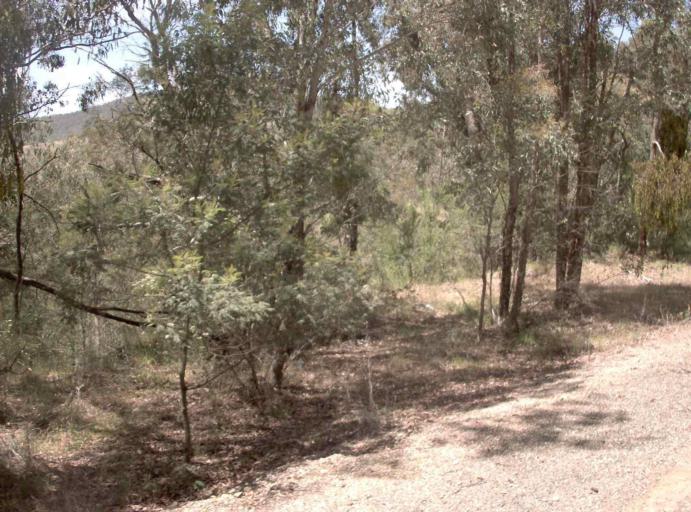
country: AU
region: Victoria
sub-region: East Gippsland
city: Bairnsdale
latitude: -37.4185
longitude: 147.8326
